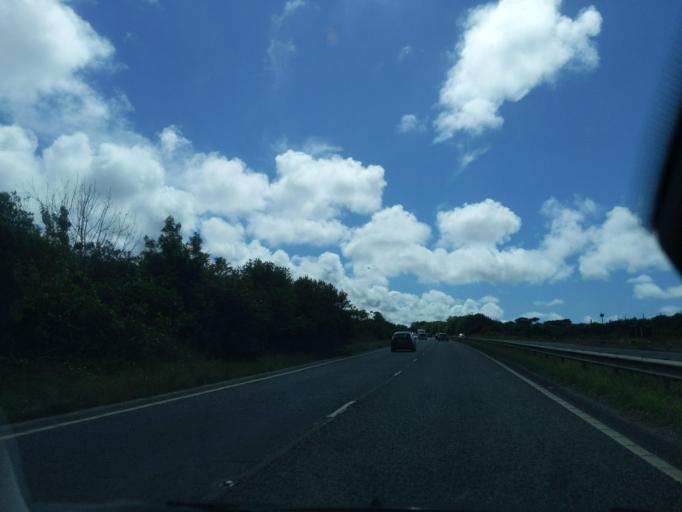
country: GB
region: England
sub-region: Cornwall
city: Chacewater
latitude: 50.2659
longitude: -5.1811
